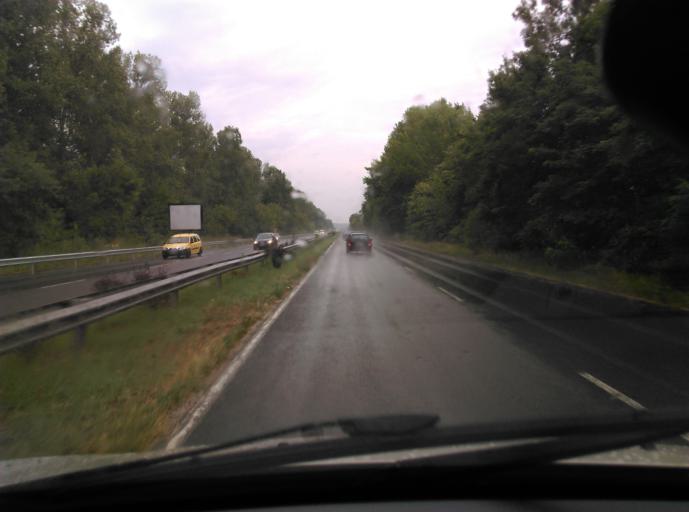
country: BG
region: Burgas
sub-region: Obshtina Burgas
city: Burgas
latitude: 42.4673
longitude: 27.4375
